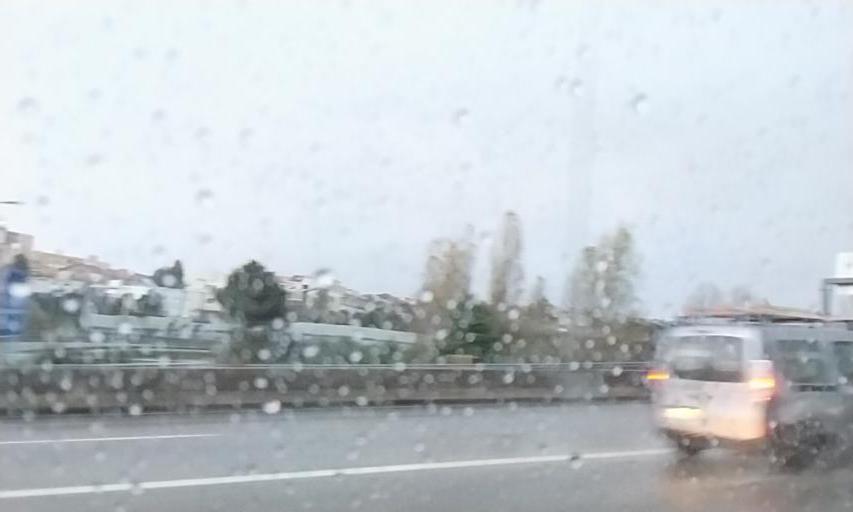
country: PT
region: Braga
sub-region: Braga
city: Braga
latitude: 41.5332
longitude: -8.4453
